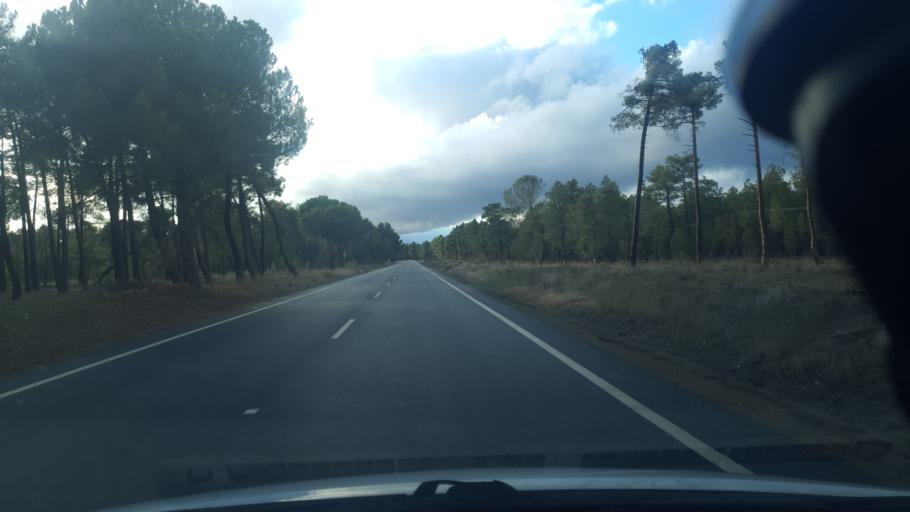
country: ES
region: Castille and Leon
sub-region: Provincia de Segovia
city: Nava de la Asuncion
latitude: 41.1558
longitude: -4.5165
